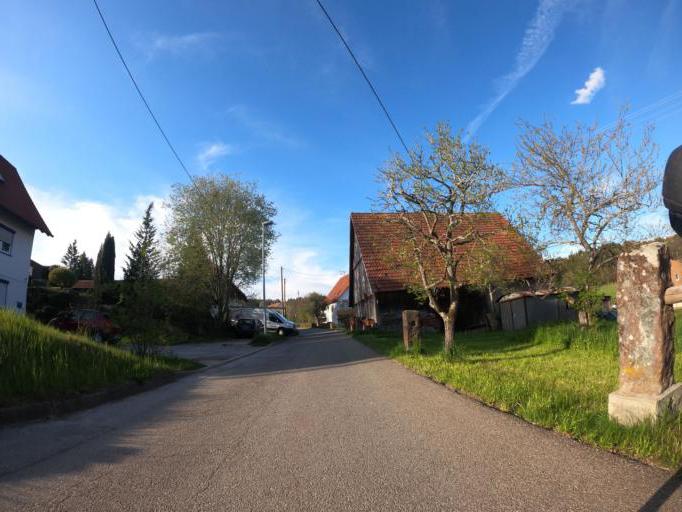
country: DE
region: Baden-Wuerttemberg
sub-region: Karlsruhe Region
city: Oberreichenbach
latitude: 48.7118
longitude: 8.6650
